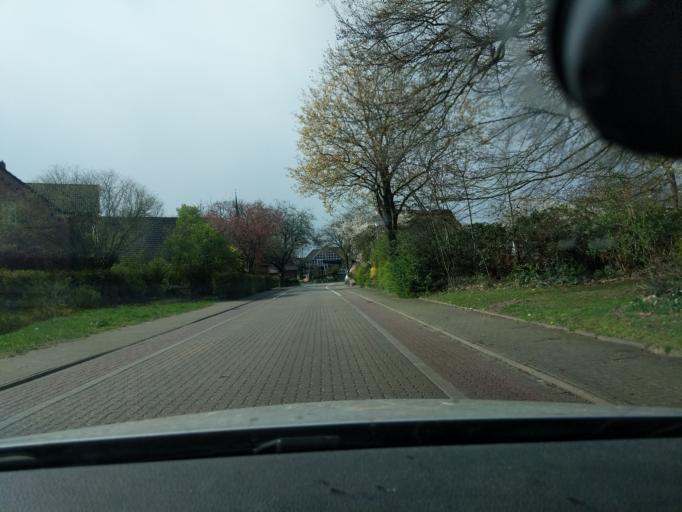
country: DE
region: Lower Saxony
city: Bargstedt
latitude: 53.4590
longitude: 9.4501
